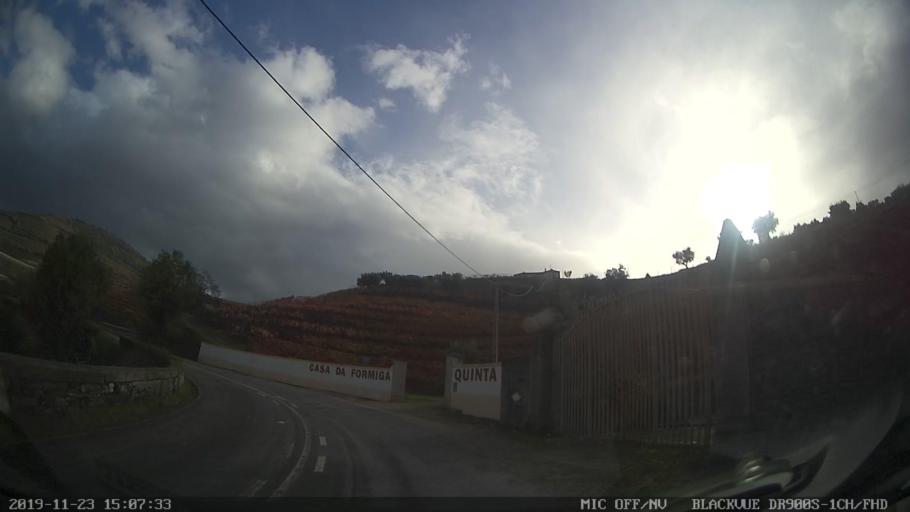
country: PT
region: Vila Real
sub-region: Peso da Regua
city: Peso da Regua
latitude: 41.1491
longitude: -7.7829
